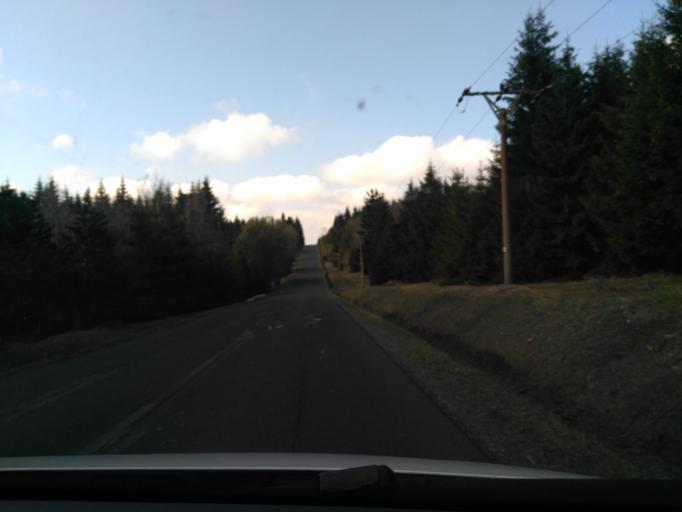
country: CZ
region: Ustecky
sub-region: Okres Chomutov
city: Kovarska
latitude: 50.4512
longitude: 13.0766
